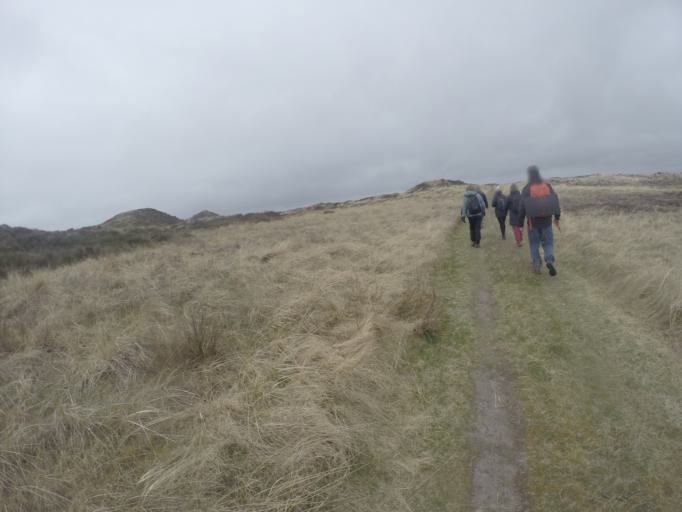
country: DK
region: North Denmark
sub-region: Thisted Kommune
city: Hurup
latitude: 56.8572
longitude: 8.2900
